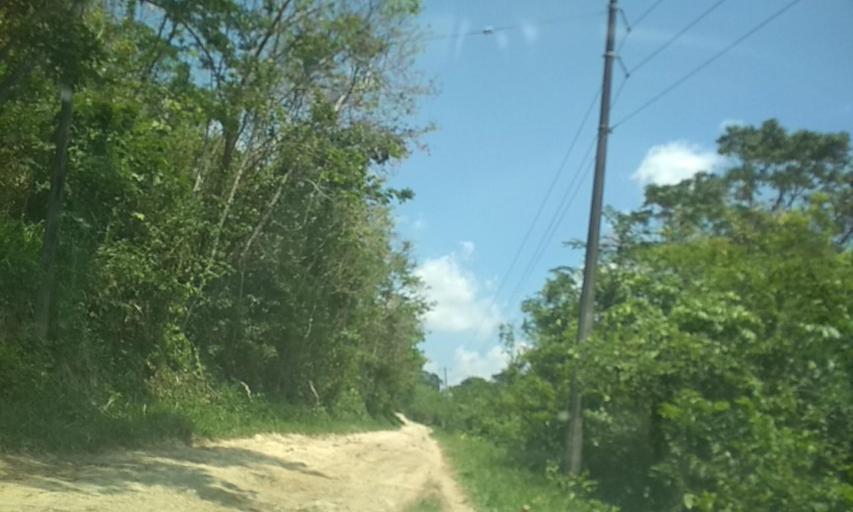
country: MX
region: Chiapas
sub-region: Tecpatan
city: Raudales Malpaso
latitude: 17.3020
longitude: -93.8252
